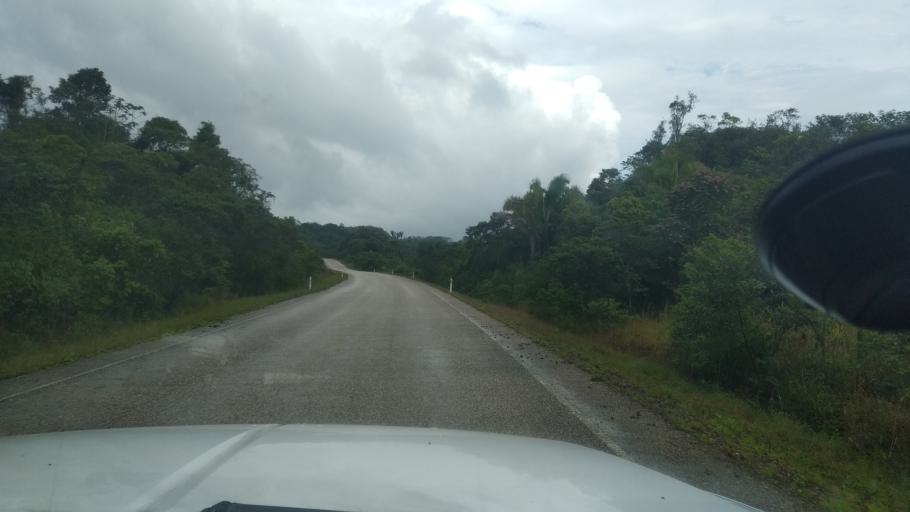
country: GT
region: Peten
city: San Luis
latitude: 16.1891
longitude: -89.1753
